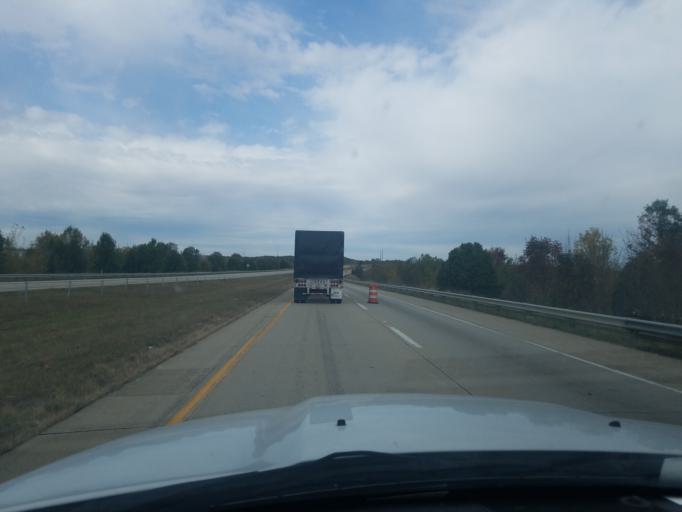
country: US
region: Indiana
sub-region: Vanderburgh County
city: Melody Hill
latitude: 38.1137
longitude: -87.4781
